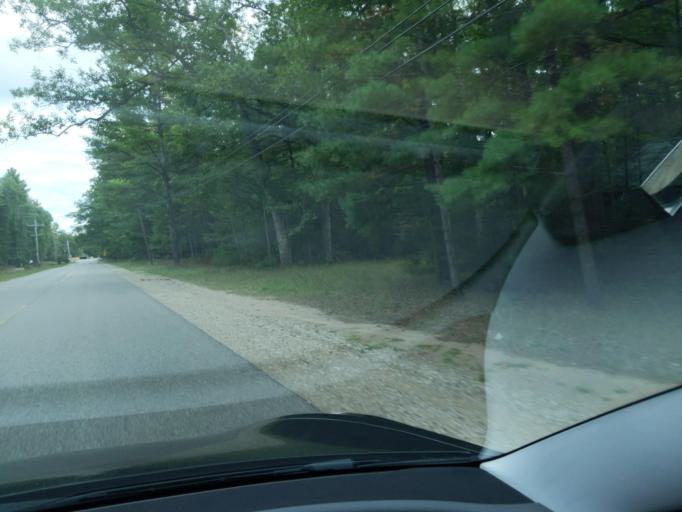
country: US
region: Michigan
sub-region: Kalkaska County
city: Rapid City
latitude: 44.8483
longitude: -85.3105
